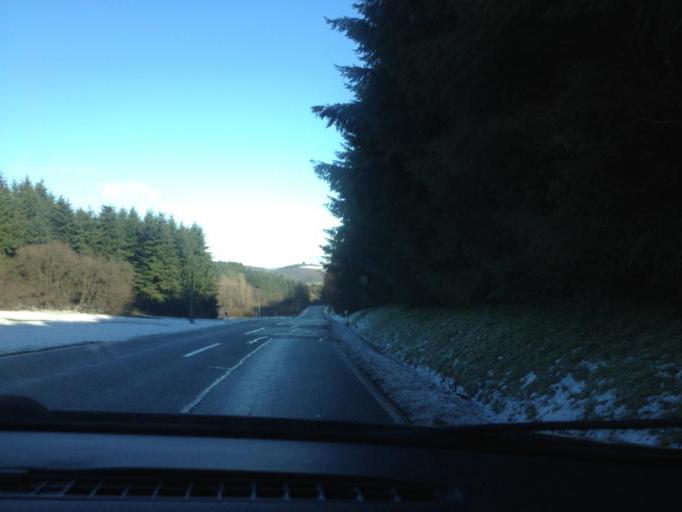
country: DE
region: Saarland
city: Freisen
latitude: 49.5370
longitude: 7.2264
